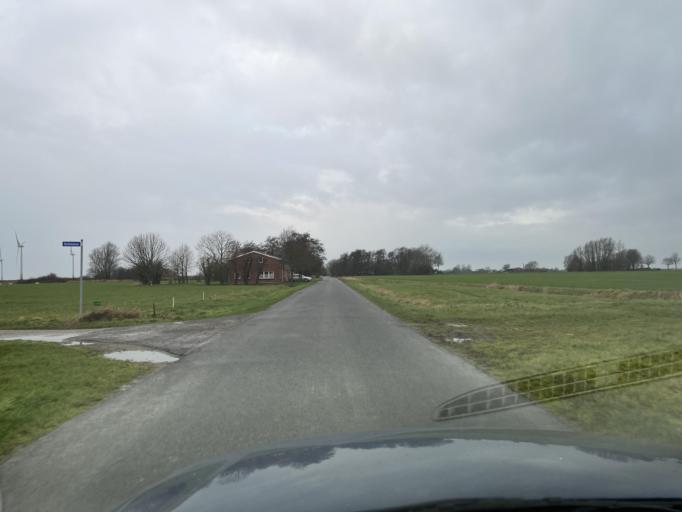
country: DE
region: Schleswig-Holstein
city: Hillgroven
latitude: 54.2167
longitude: 8.8803
